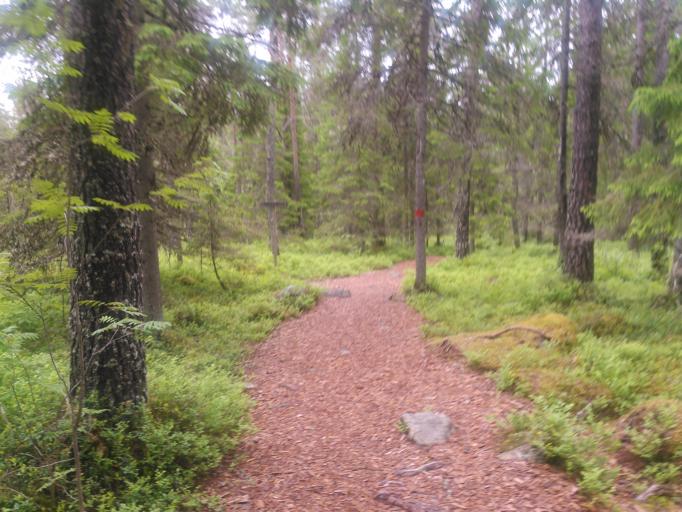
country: SE
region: Vaesterbotten
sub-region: Umea Kommun
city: Holmsund
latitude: 63.7820
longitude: 20.3481
